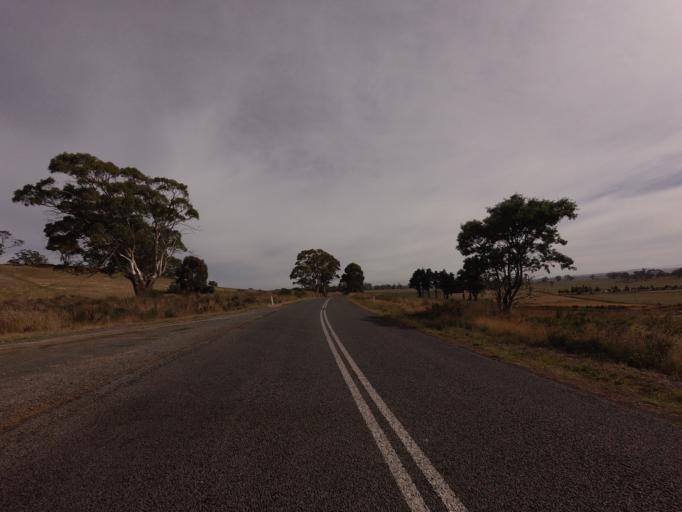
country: AU
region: Tasmania
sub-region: Brighton
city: Bridgewater
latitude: -42.3701
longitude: 147.4167
